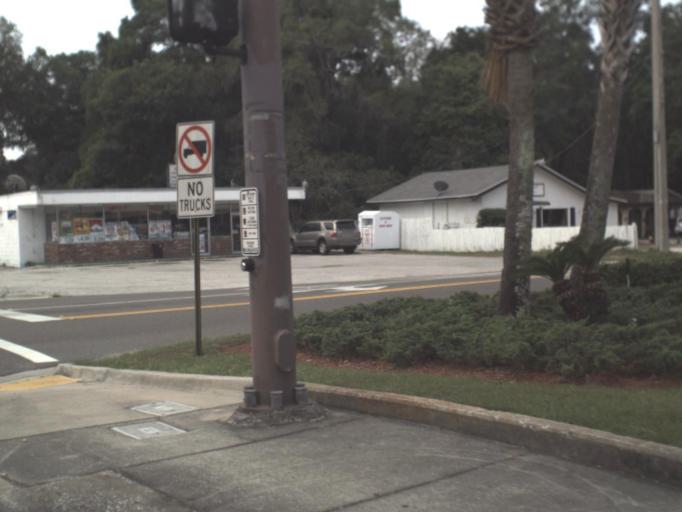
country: US
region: Florida
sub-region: Clay County
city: Orange Park
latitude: 30.1630
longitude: -81.7011
